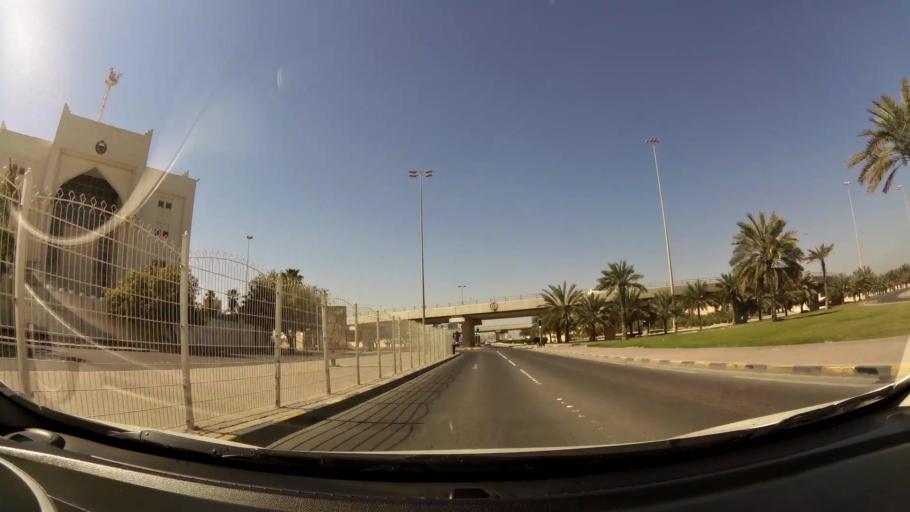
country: BH
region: Muharraq
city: Al Muharraq
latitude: 26.2515
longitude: 50.6074
